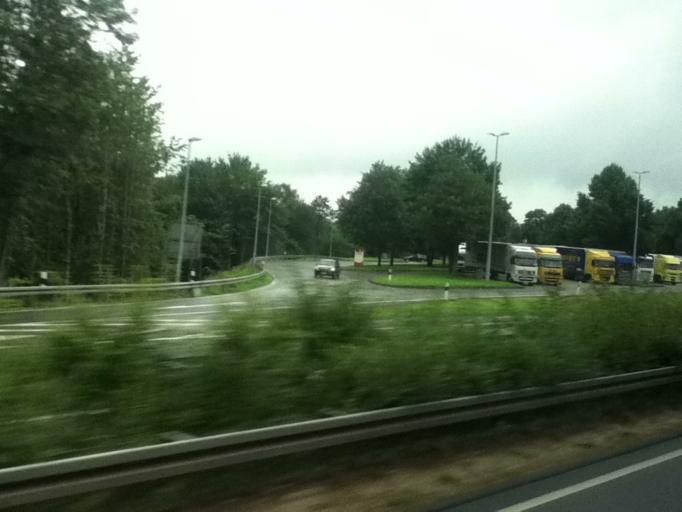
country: DE
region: North Rhine-Westphalia
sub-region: Regierungsbezirk Koln
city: Overath
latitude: 50.9502
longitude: 7.3185
